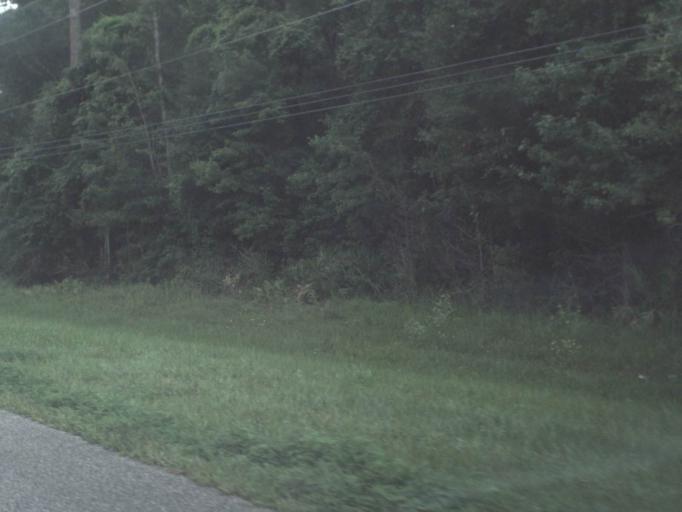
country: US
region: Florida
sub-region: Nassau County
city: Nassau Village-Ratliff
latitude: 30.4776
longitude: -81.7820
